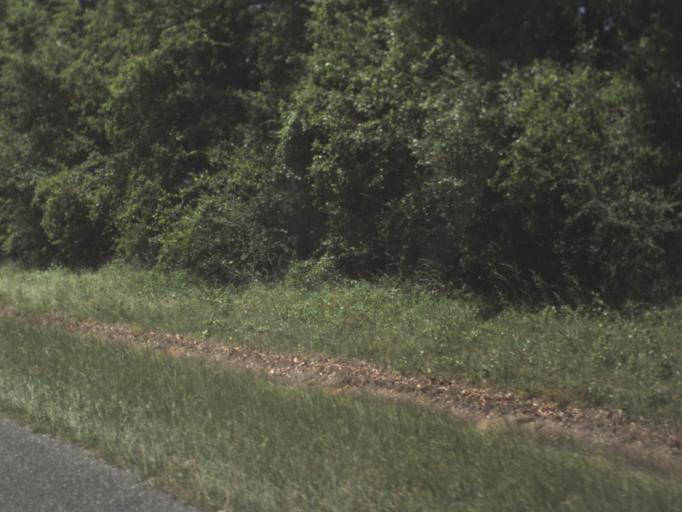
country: US
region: Florida
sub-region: Jefferson County
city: Monticello
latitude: 30.6343
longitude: -83.8733
